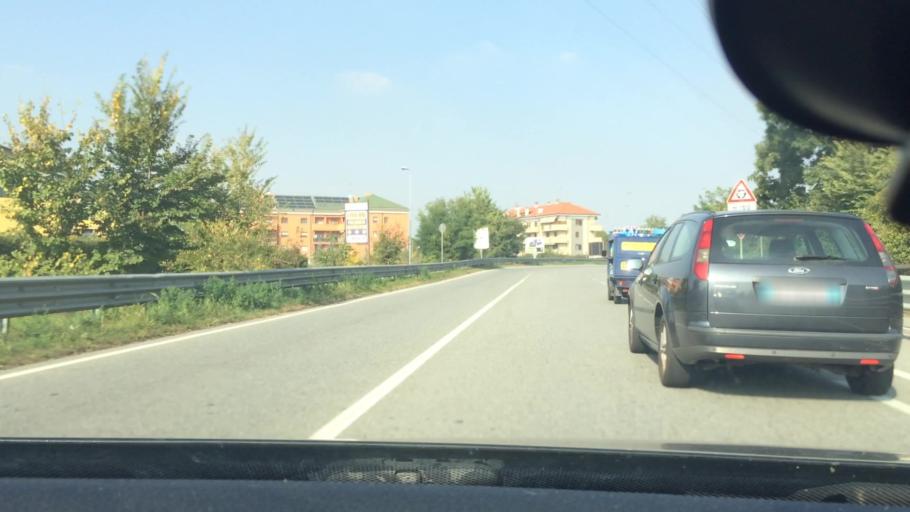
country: IT
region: Lombardy
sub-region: Citta metropolitana di Milano
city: Cornaredo
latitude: 45.5122
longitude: 9.0310
